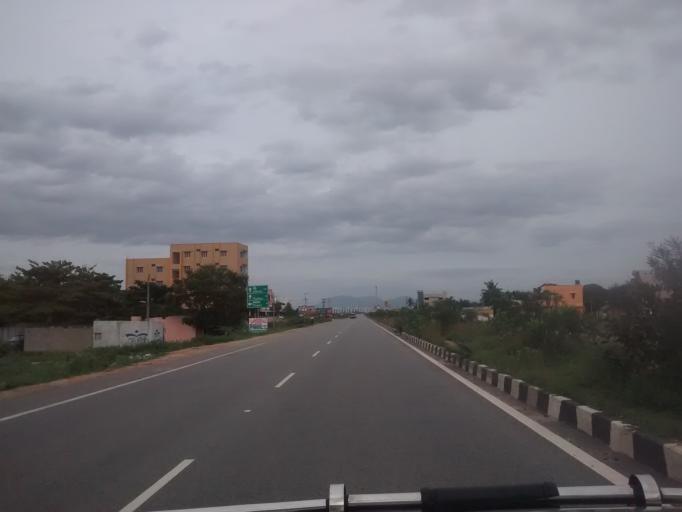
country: IN
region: Andhra Pradesh
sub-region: Chittoor
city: Tirupati
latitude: 13.6046
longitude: 79.3935
